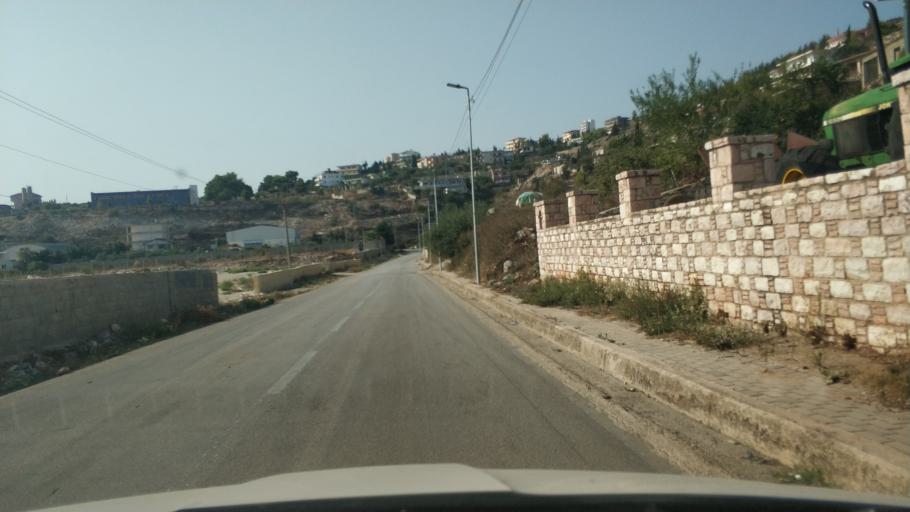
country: AL
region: Vlore
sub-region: Rrethi i Sarandes
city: Sarande
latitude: 39.8483
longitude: 20.0302
